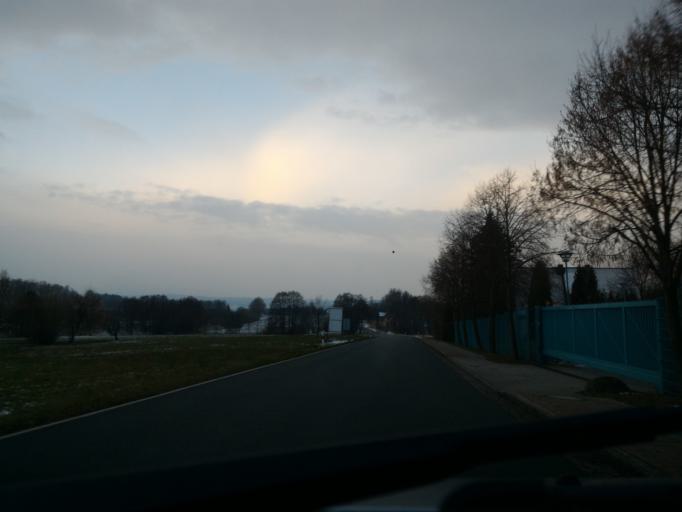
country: DE
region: Saxony
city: Leutersdorf
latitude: 50.9512
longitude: 14.6360
